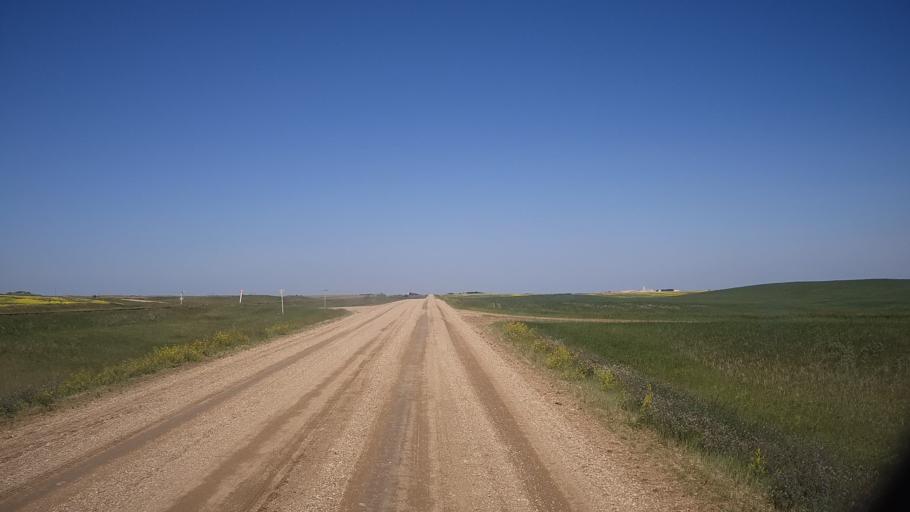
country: CA
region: Saskatchewan
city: Watrous
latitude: 51.8524
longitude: -105.9397
